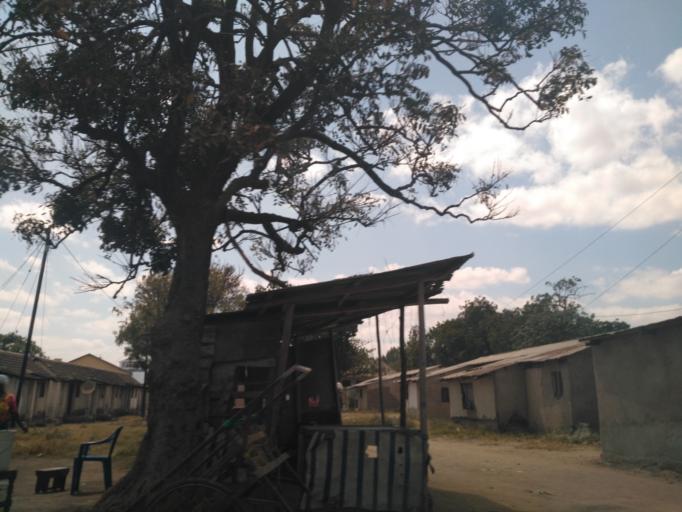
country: TZ
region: Dodoma
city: Dodoma
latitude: -6.1803
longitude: 35.7419
